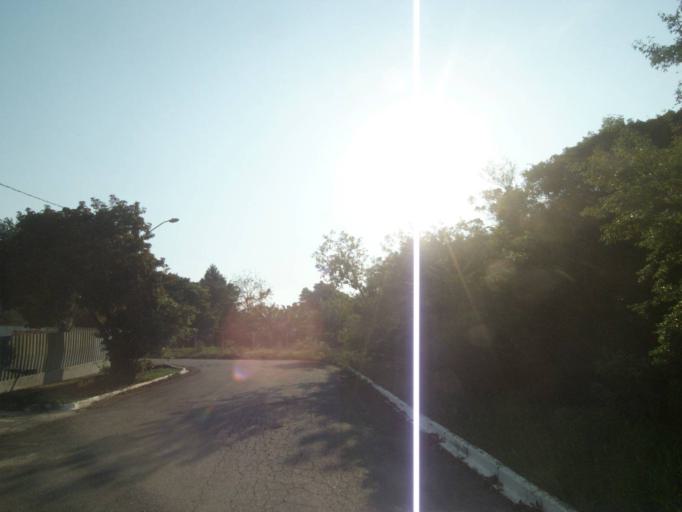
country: BR
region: Parana
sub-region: Curitiba
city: Curitiba
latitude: -25.4919
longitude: -49.2665
